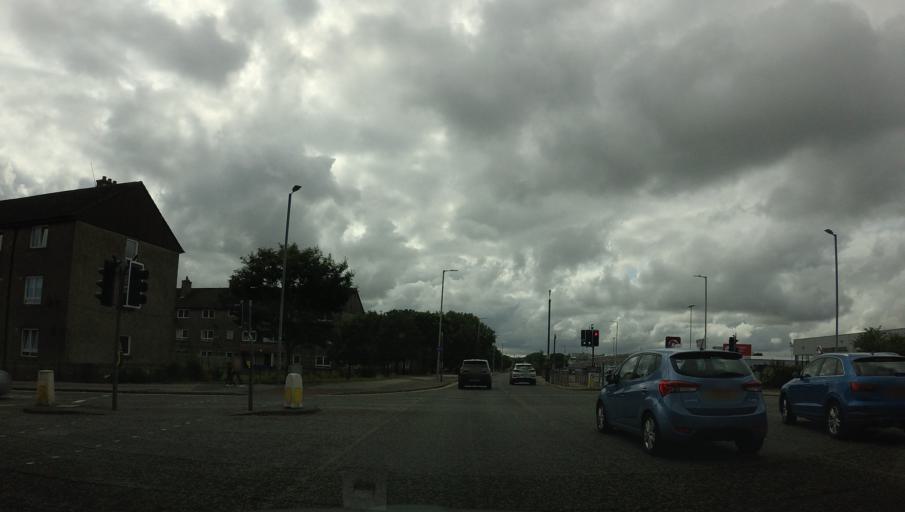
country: GB
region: Scotland
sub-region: Aberdeen City
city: Cults
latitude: 57.1516
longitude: -2.1533
